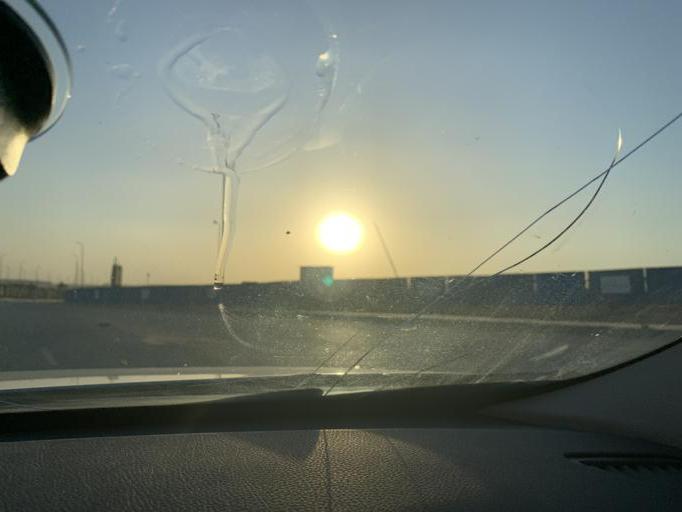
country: EG
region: Muhafazat al Qalyubiyah
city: Al Khankah
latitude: 30.0270
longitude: 31.5591
